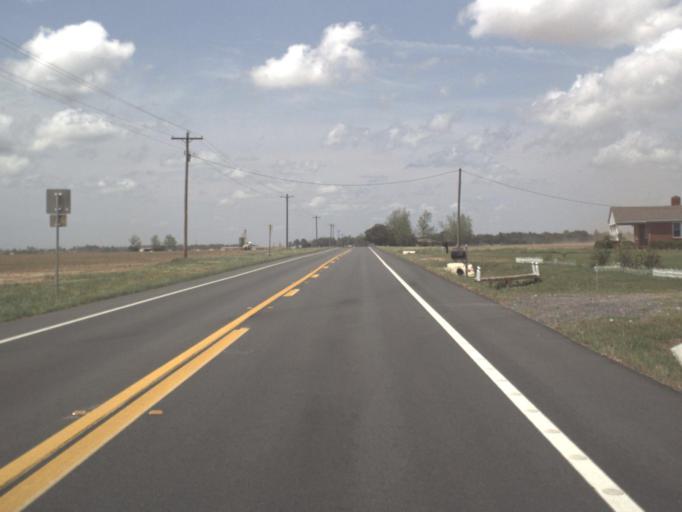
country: US
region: Florida
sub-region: Escambia County
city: Century
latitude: 30.8809
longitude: -87.1619
